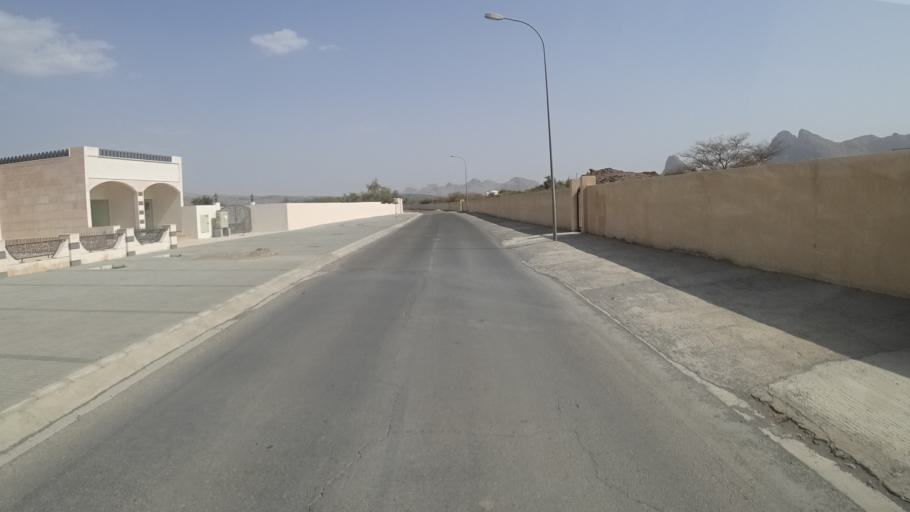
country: OM
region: Muhafazat ad Dakhiliyah
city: Bahla'
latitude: 23.1081
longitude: 57.2952
